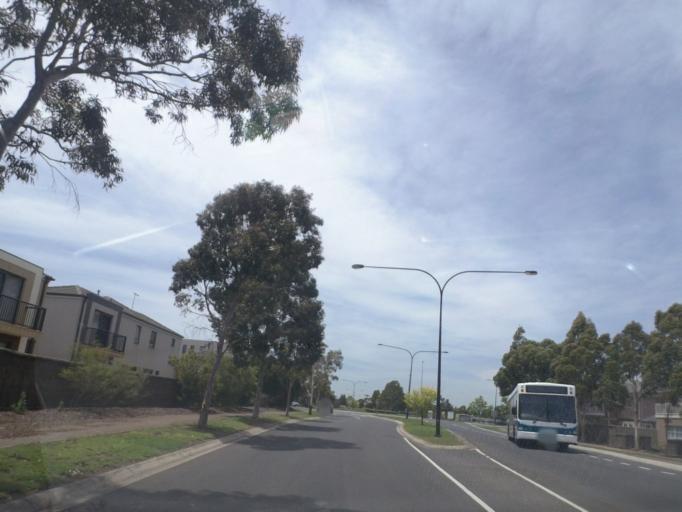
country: AU
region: Victoria
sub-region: Melton
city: Caroline Springs
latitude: -37.7430
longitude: 144.7346
